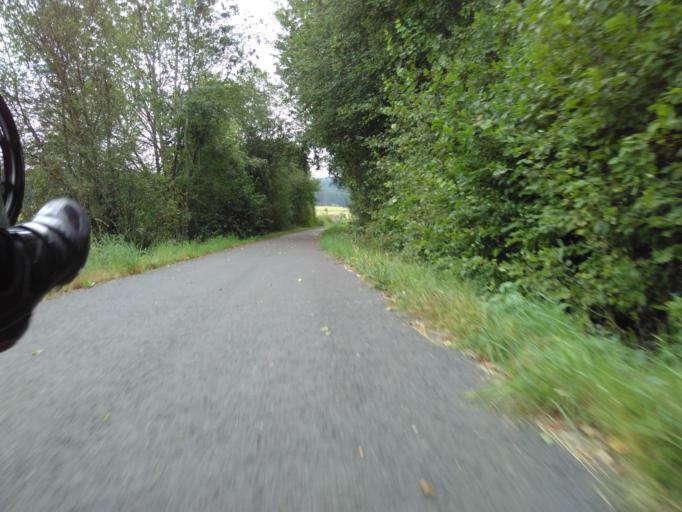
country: DE
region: Thuringia
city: Gehren
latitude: 50.6427
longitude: 11.0119
